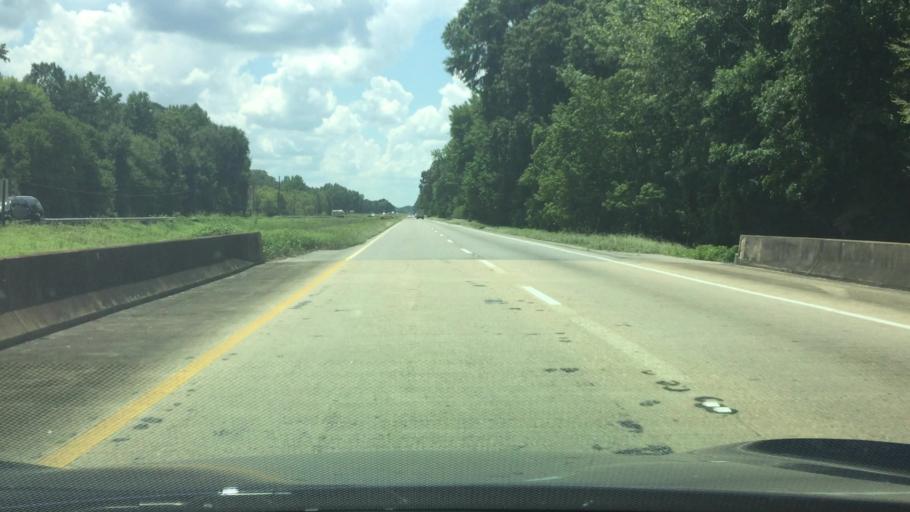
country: US
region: Alabama
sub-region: Montgomery County
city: Pike Road
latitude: 32.1860
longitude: -86.1175
